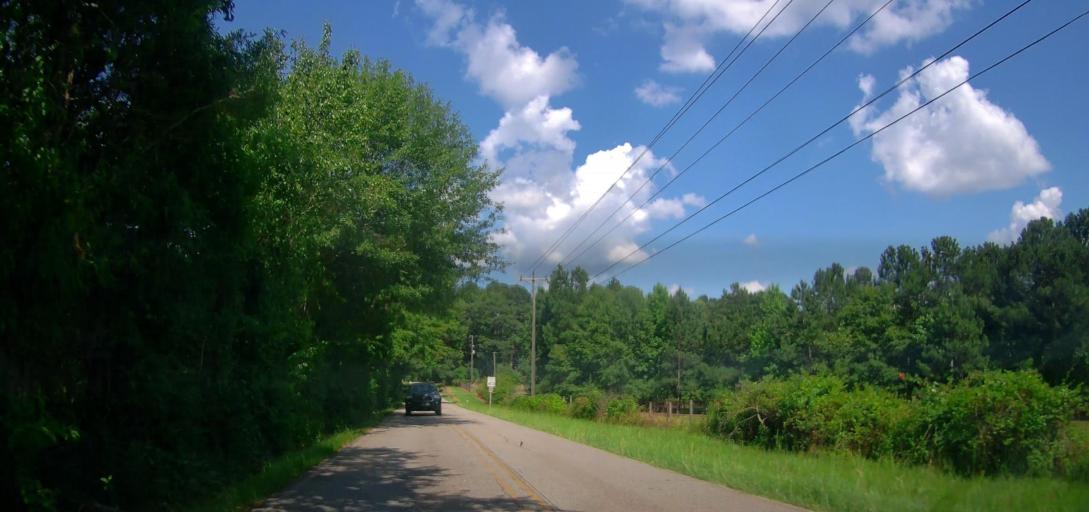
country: US
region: Georgia
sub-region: Spalding County
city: East Griffin
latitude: 33.2314
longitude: -84.1352
